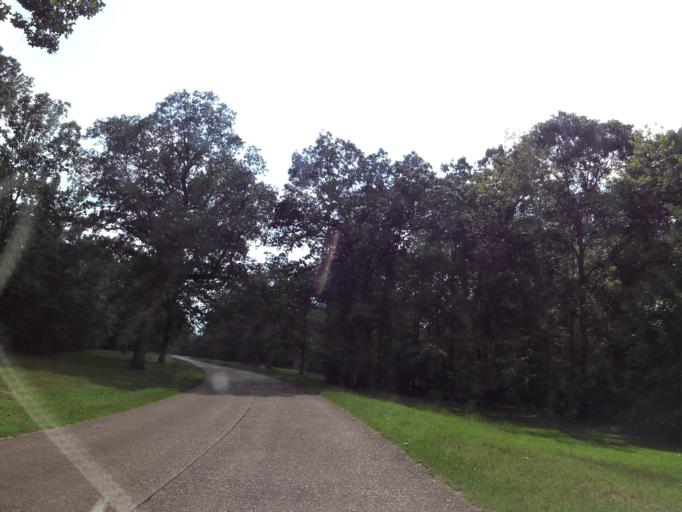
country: US
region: Tennessee
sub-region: Hardin County
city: Crump
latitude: 35.1475
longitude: -88.3306
